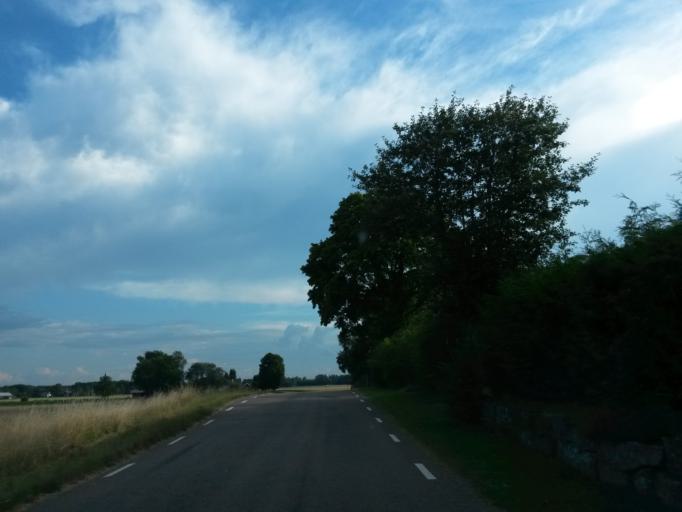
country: SE
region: Vaestra Goetaland
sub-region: Grastorps Kommun
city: Graestorp
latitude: 58.3324
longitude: 12.7609
